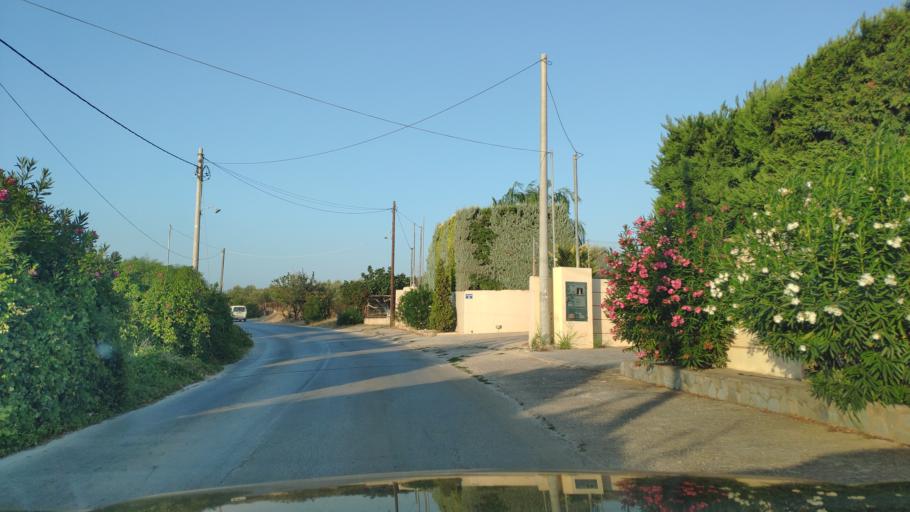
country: GR
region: Attica
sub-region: Nomarchia Anatolikis Attikis
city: Markopoulo
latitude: 37.8984
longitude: 23.9552
